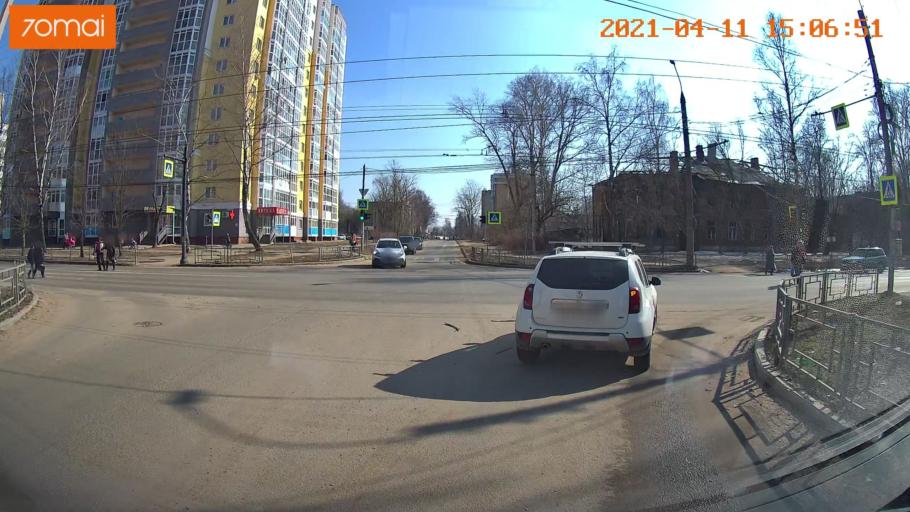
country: RU
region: Ivanovo
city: Bogorodskoye
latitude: 57.0177
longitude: 41.0171
